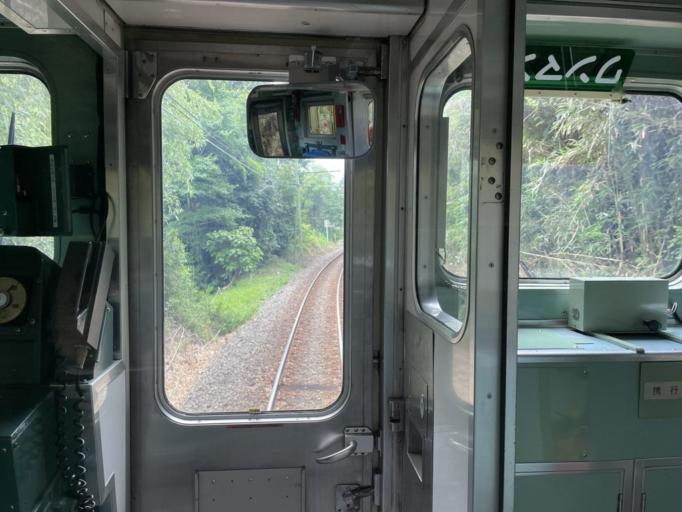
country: JP
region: Gunma
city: Takasaki
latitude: 36.2830
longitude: 139.0322
